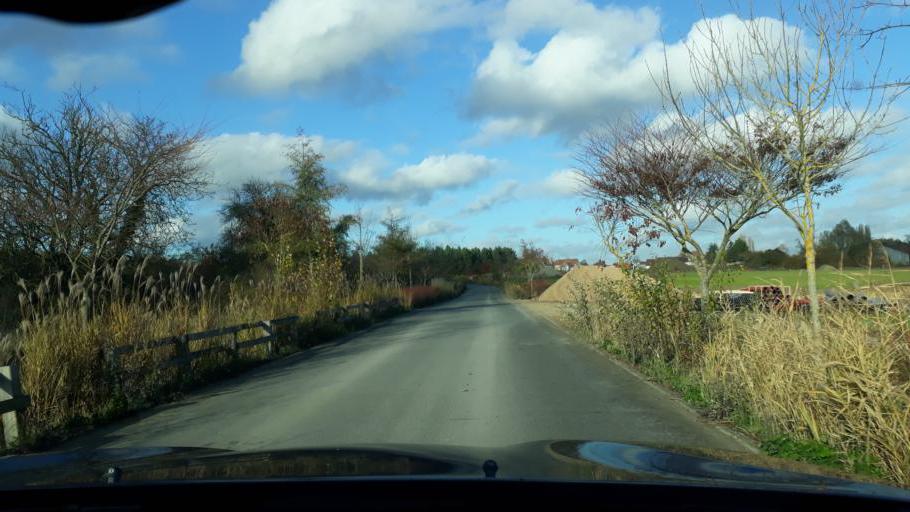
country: FR
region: Centre
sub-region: Departement du Loiret
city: Marigny-les-Usages
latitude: 47.9466
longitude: 2.0096
